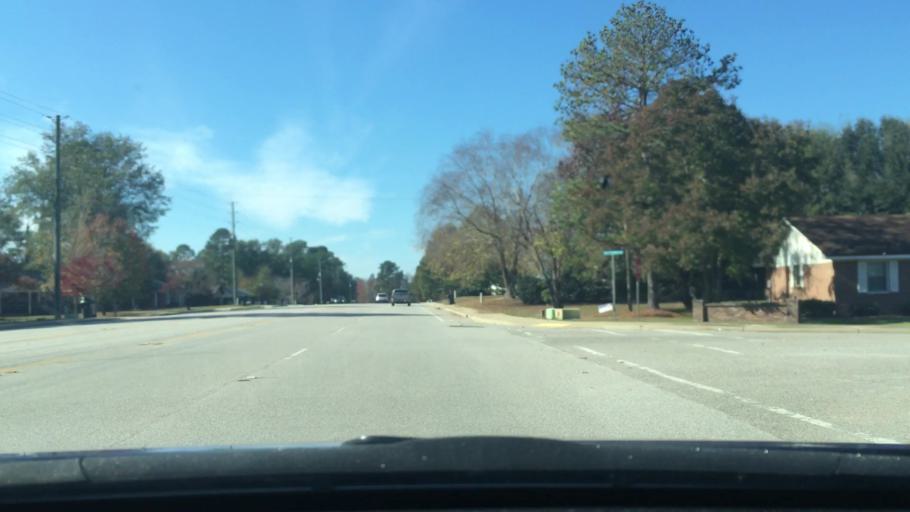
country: US
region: South Carolina
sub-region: Sumter County
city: Cane Savannah
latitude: 33.8966
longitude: -80.4030
